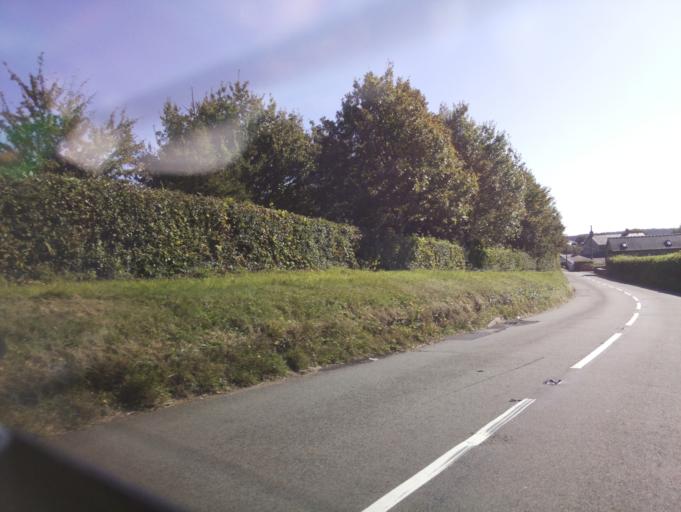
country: GB
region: Wales
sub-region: Torfaen County Borough
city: Cwmbran
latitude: 51.6314
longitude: -3.0518
